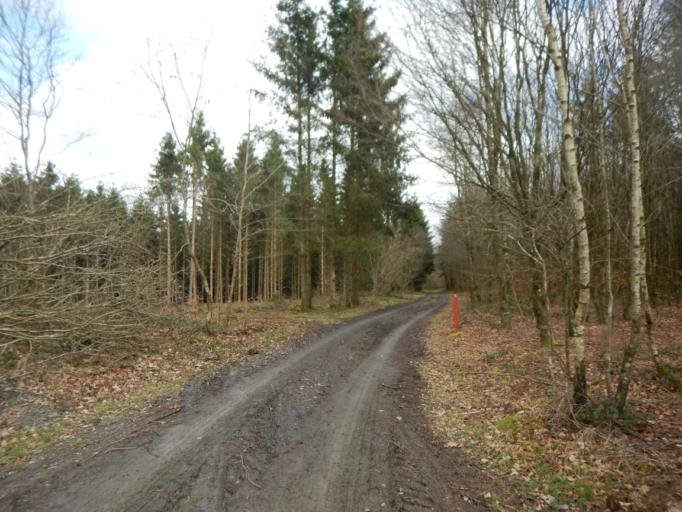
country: LU
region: Diekirch
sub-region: Canton de Wiltz
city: Winseler
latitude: 49.9306
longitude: 5.8985
